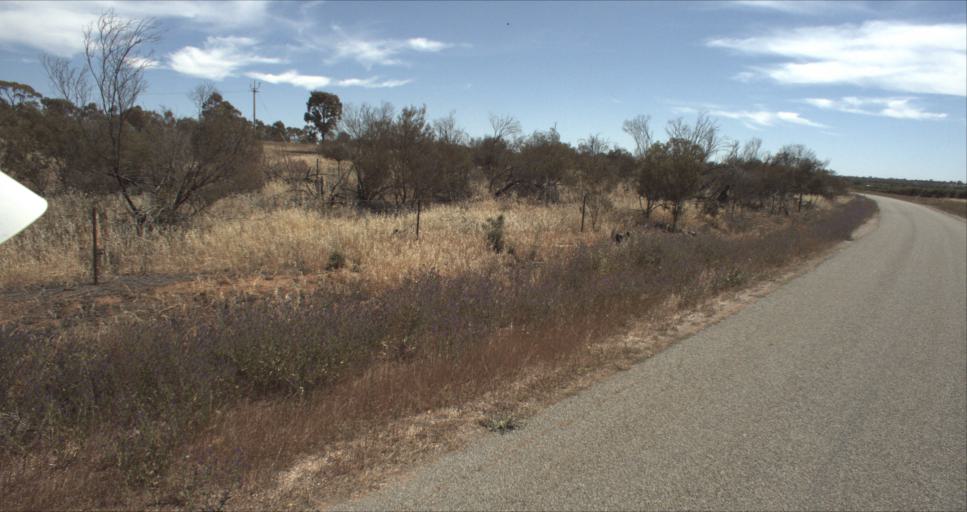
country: AU
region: New South Wales
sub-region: Leeton
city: Leeton
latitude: -34.5939
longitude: 146.4743
